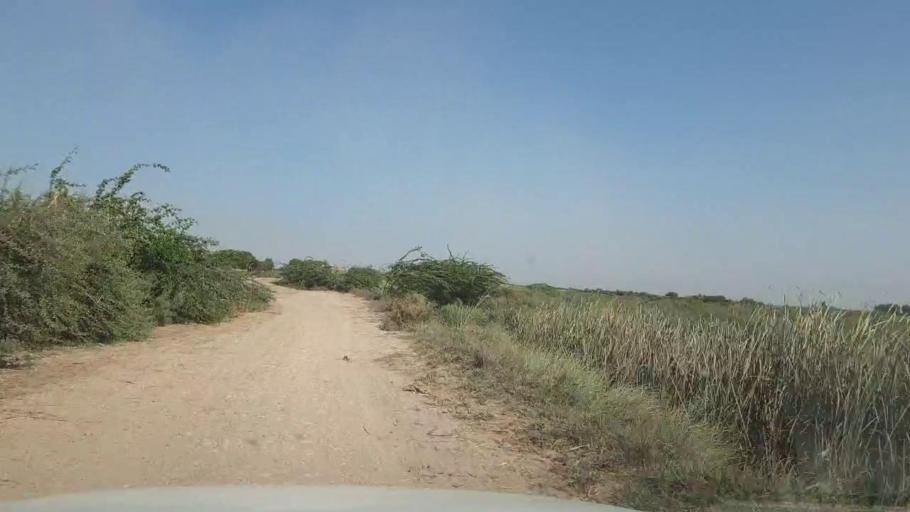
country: PK
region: Sindh
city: Mirpur Sakro
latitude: 24.4114
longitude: 67.7613
